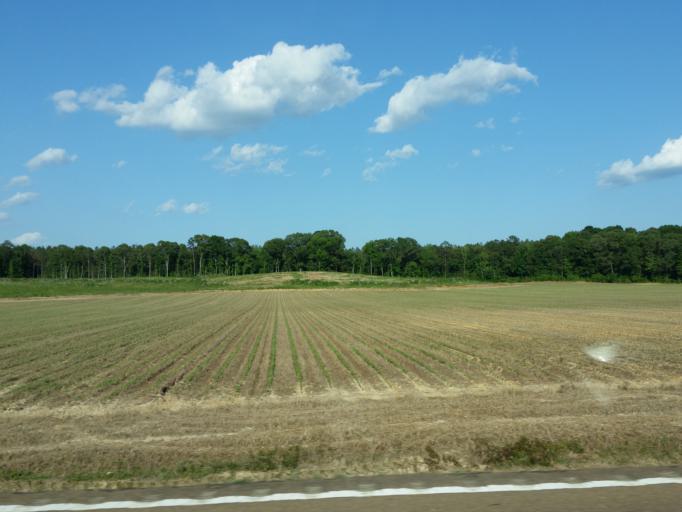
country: US
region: Mississippi
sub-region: Calhoun County
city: Calhoun City
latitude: 33.7820
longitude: -89.3641
